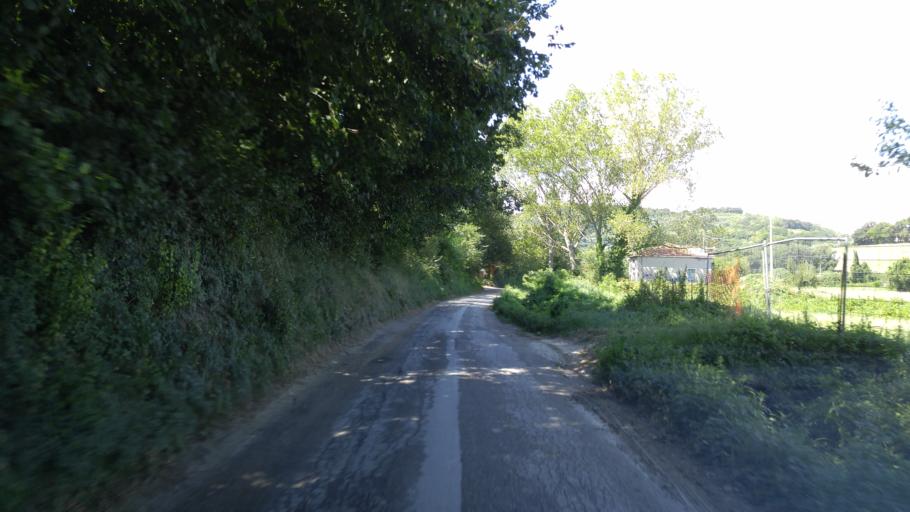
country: IT
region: The Marches
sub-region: Provincia di Pesaro e Urbino
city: Centinarola
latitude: 43.8307
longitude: 12.9839
